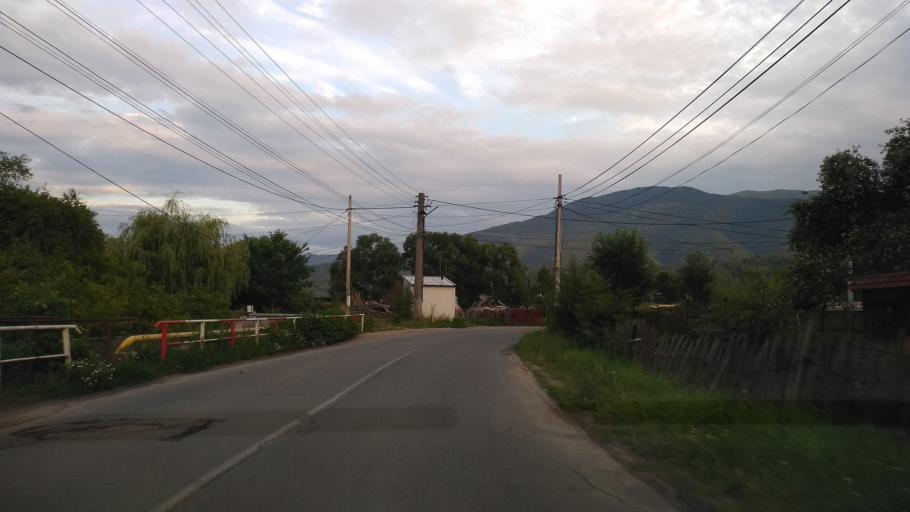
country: RO
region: Hunedoara
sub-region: Comuna Aninoasa
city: Iscroni
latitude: 45.3861
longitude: 23.3273
